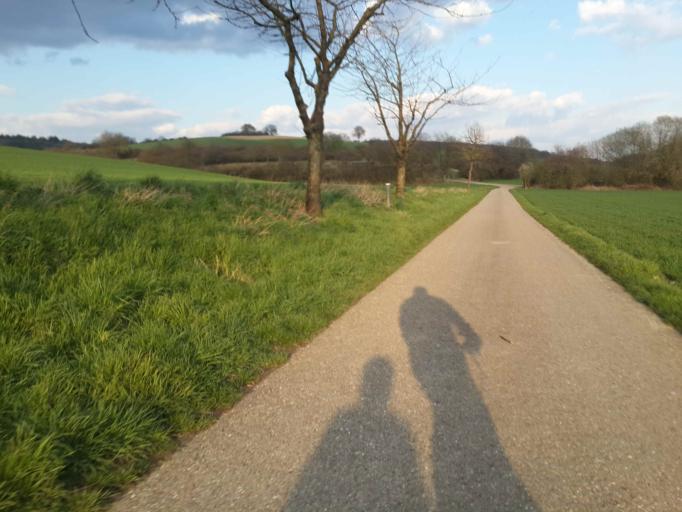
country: DE
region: Baden-Wuerttemberg
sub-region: Regierungsbezirk Stuttgart
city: Ittlingen
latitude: 49.2338
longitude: 8.9273
